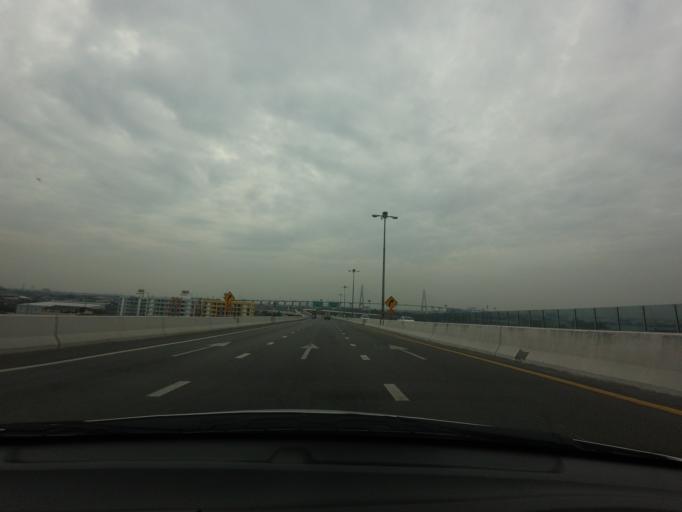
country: TH
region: Samut Prakan
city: Phra Pradaeng
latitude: 13.6511
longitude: 100.5413
